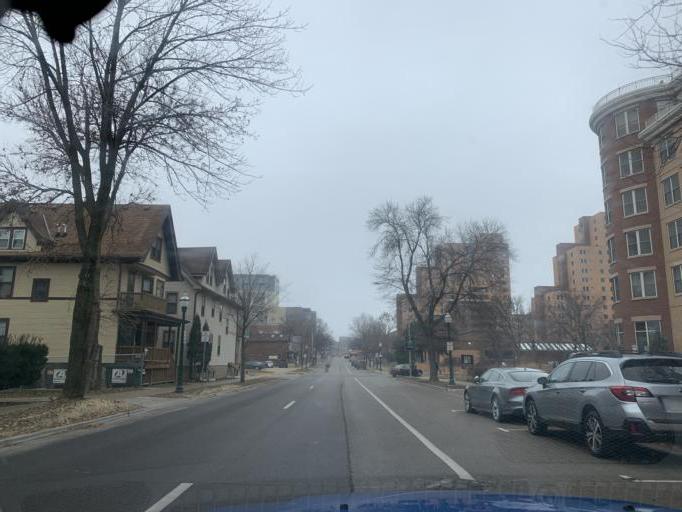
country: US
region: Wisconsin
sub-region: Dane County
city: Madison
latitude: 43.0717
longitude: -89.3893
